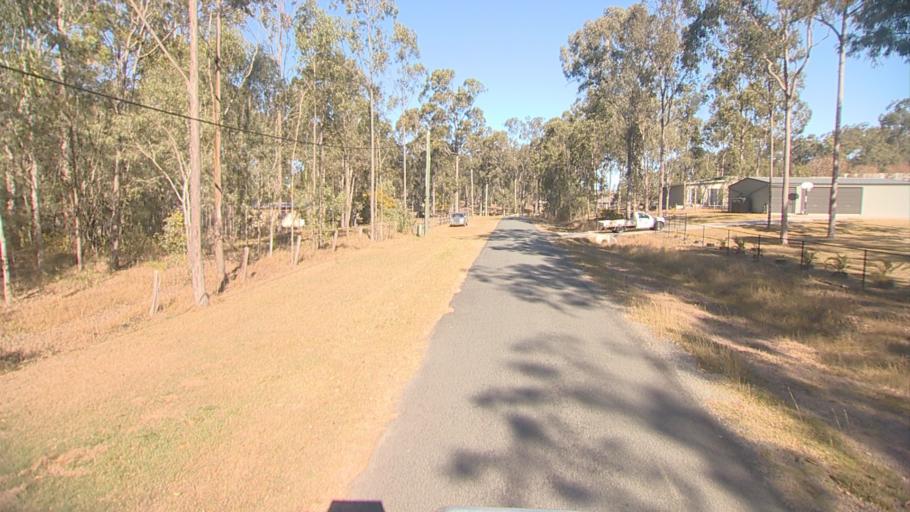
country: AU
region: Queensland
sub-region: Logan
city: North Maclean
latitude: -27.8212
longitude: 152.9816
